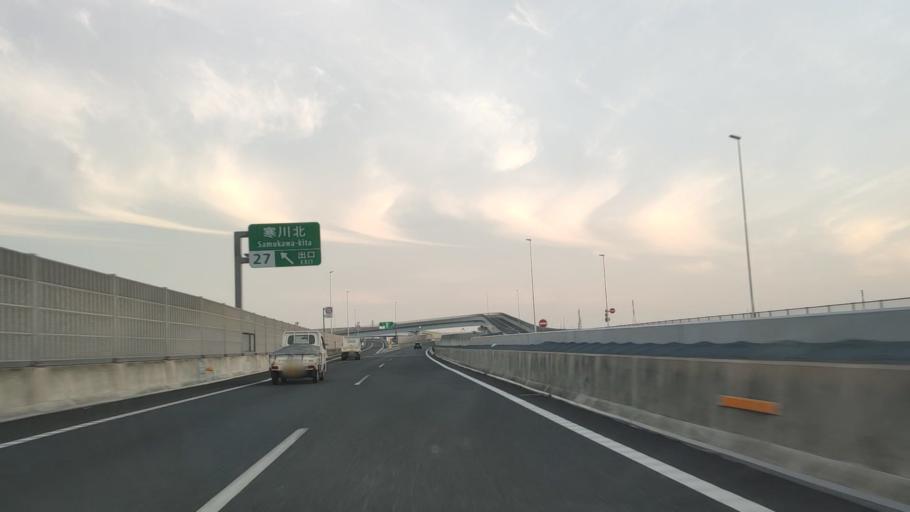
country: JP
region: Kanagawa
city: Atsugi
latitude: 35.3861
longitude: 139.3785
